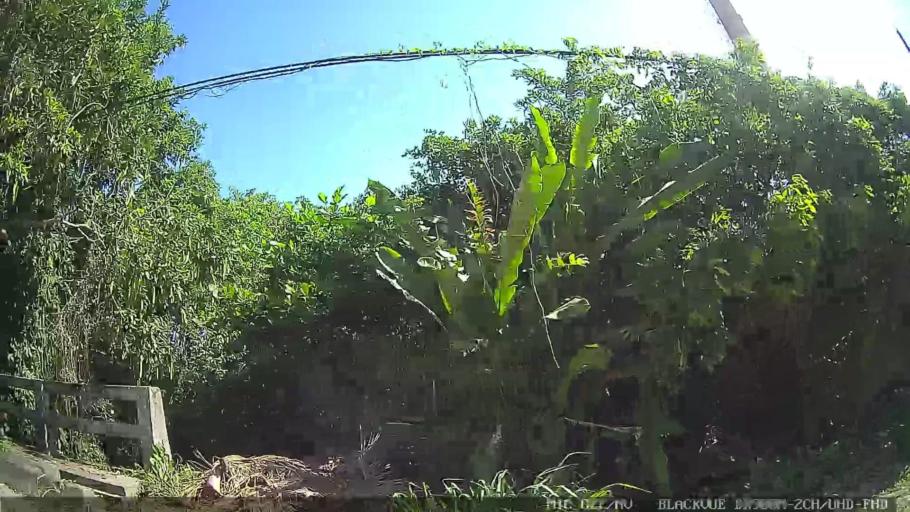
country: BR
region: Sao Paulo
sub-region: Peruibe
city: Peruibe
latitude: -24.3136
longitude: -46.9971
